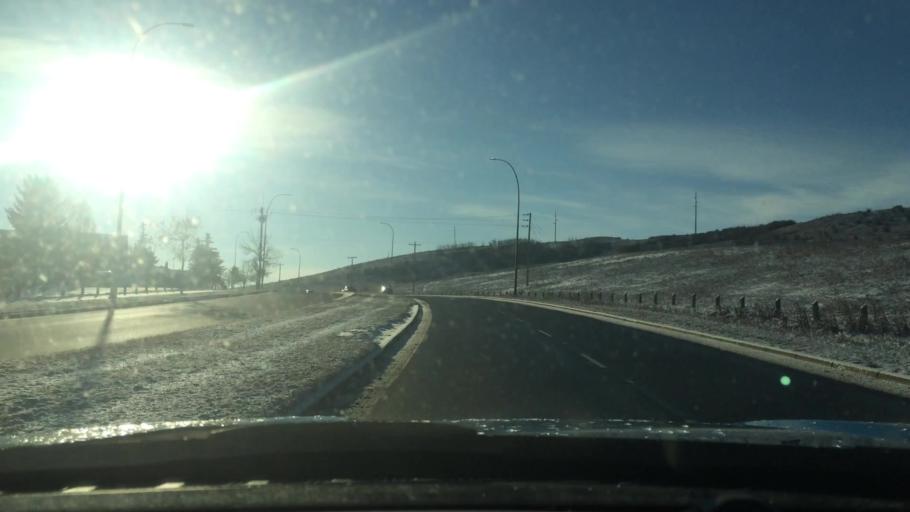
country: CA
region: Alberta
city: Calgary
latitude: 51.1297
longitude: -114.1057
